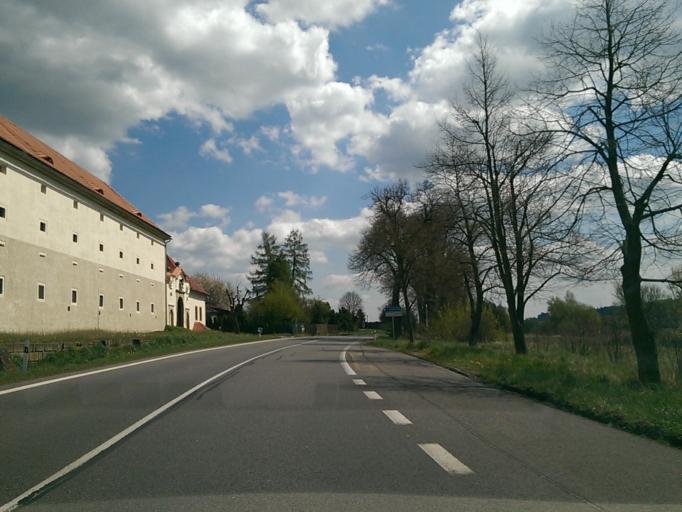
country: CZ
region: Liberecky
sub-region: Okres Semily
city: Turnov
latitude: 50.5702
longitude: 15.1795
